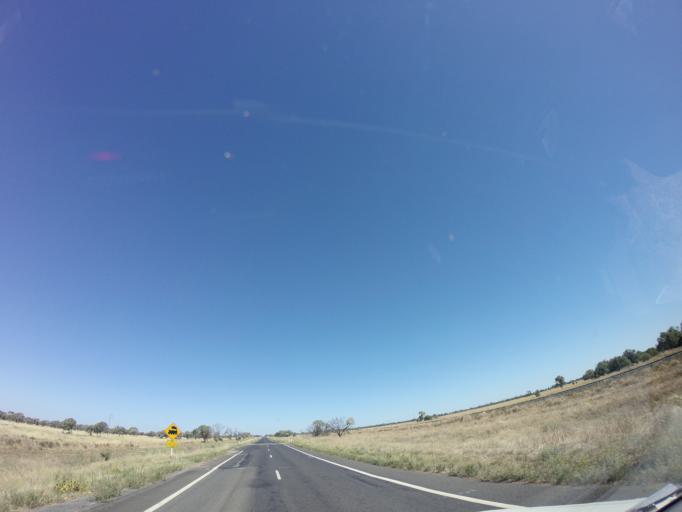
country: AU
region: New South Wales
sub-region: Bogan
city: Nyngan
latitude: -31.6099
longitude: 147.2866
